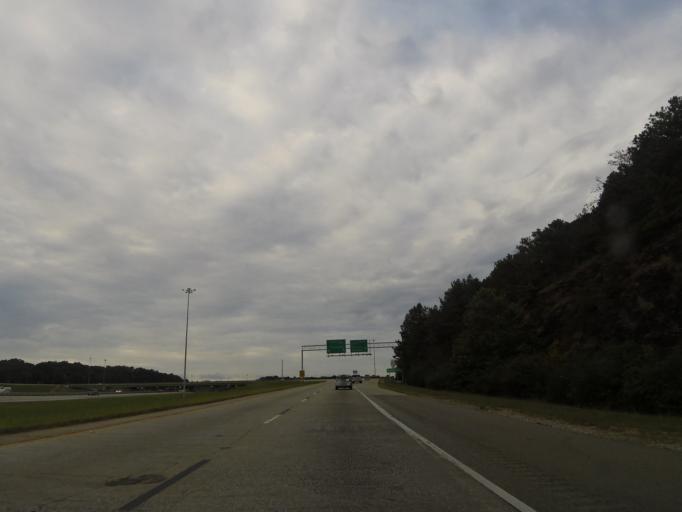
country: US
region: Alabama
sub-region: Jefferson County
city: Hoover
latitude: 33.3897
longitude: -86.7834
